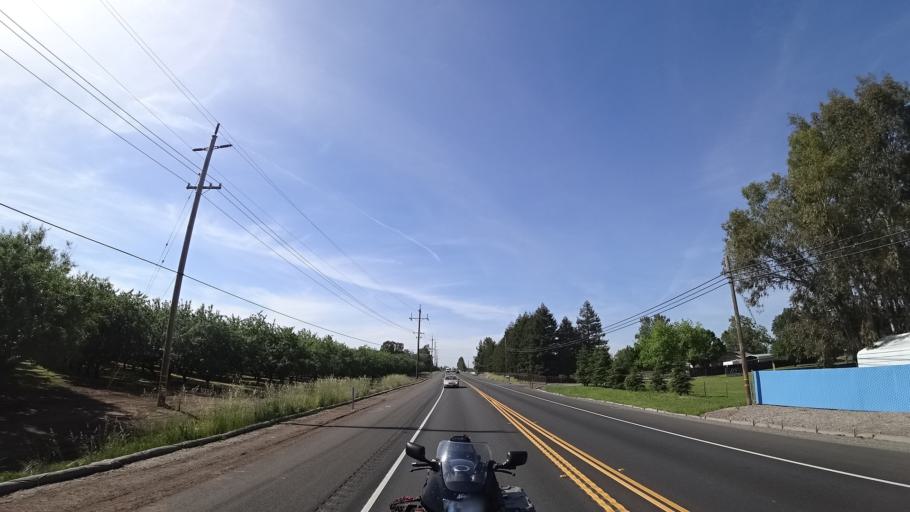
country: US
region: California
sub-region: Glenn County
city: Hamilton City
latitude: 39.8172
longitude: -121.9208
